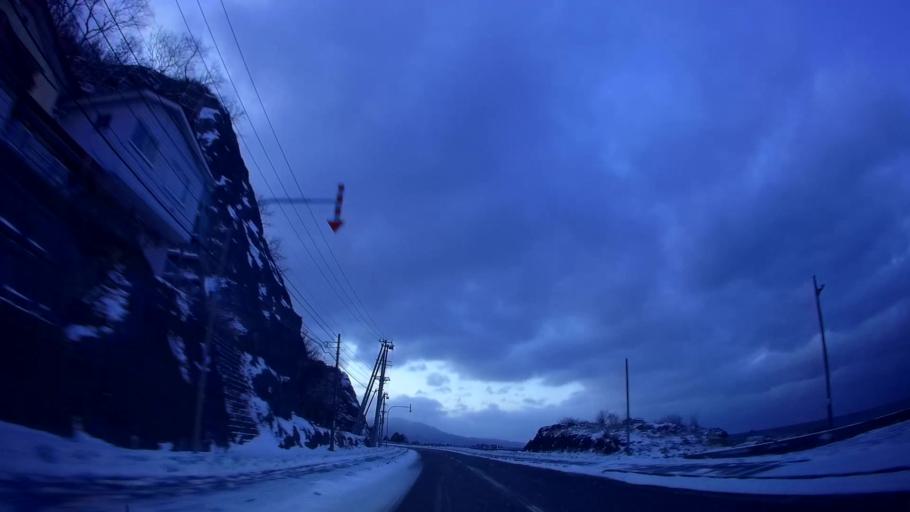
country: JP
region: Hokkaido
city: Hakodate
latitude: 41.8892
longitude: 141.0607
